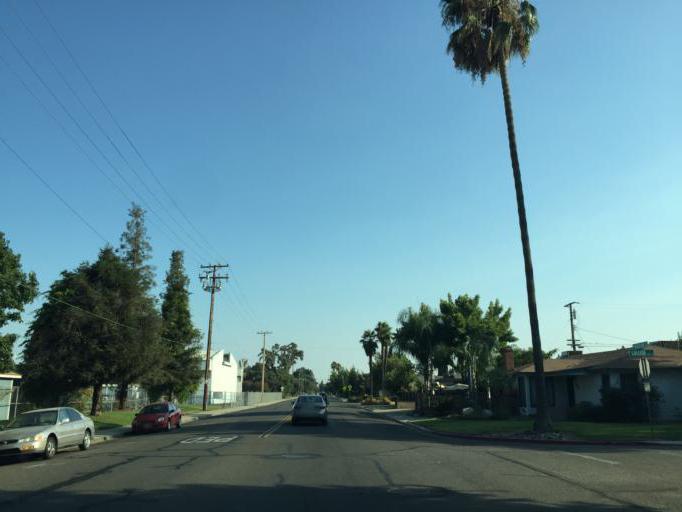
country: US
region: California
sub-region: Tulare County
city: Visalia
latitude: 36.3238
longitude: -119.3184
